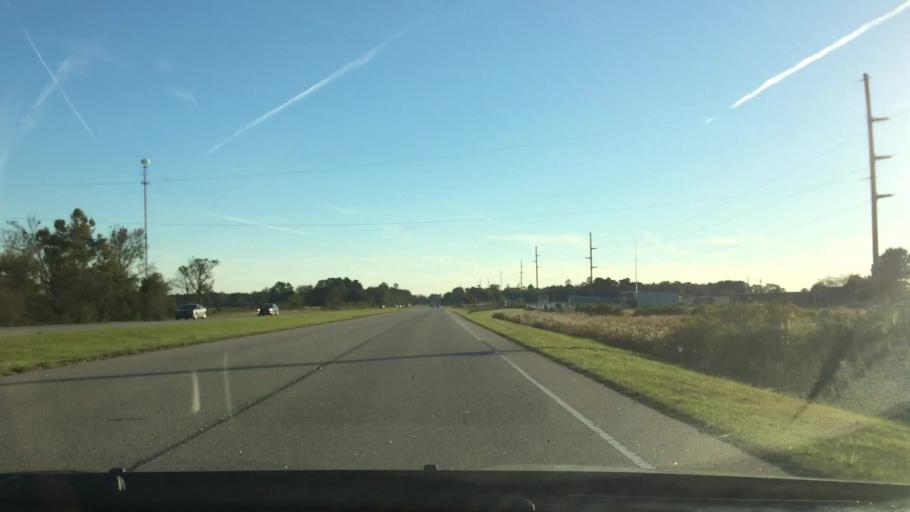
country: US
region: North Carolina
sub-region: Pitt County
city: Grifton
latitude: 35.3767
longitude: -77.4523
